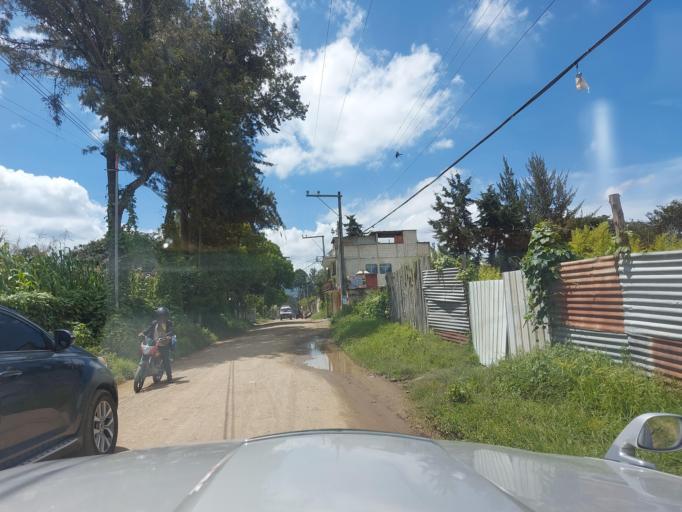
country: GT
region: Chimaltenango
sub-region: Municipio de Chimaltenango
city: Chimaltenango
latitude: 14.6466
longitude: -90.8152
